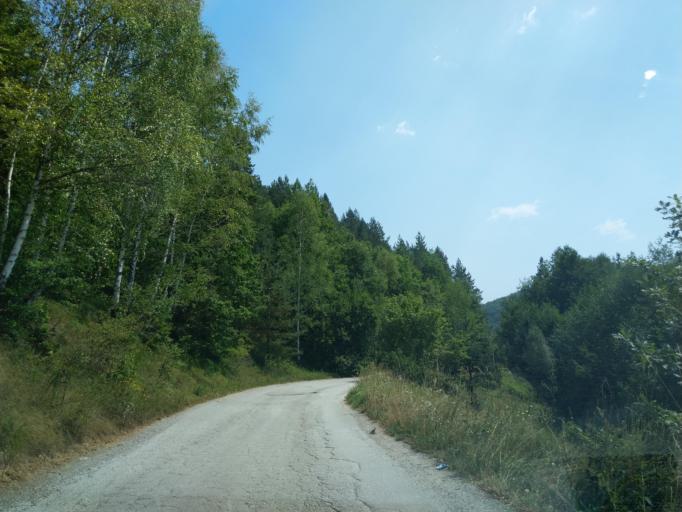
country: RS
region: Central Serbia
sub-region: Zlatiborski Okrug
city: Prijepolje
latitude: 43.3324
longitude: 19.5634
